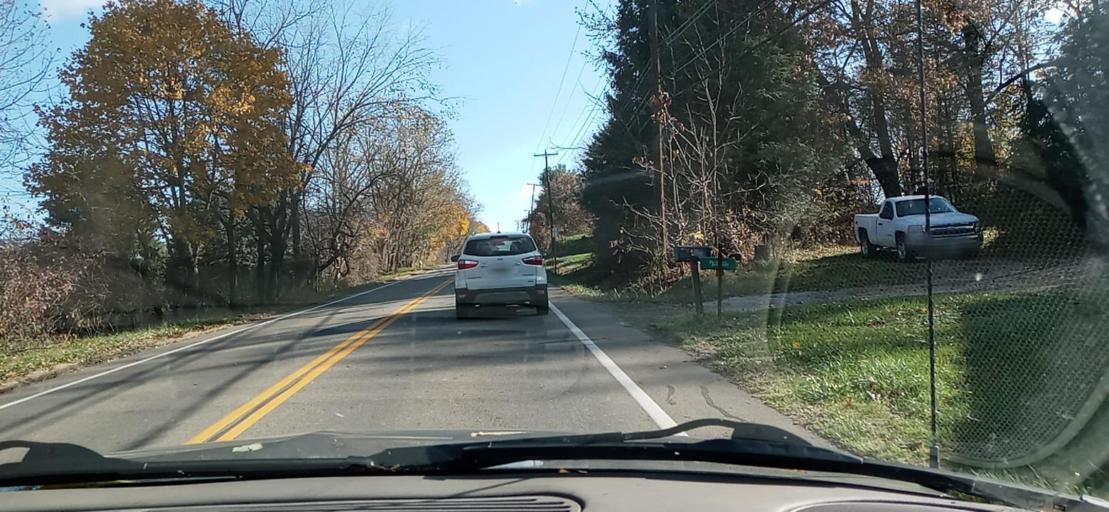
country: US
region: Ohio
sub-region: Summit County
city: Portage Lakes
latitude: 40.9978
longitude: -81.5064
